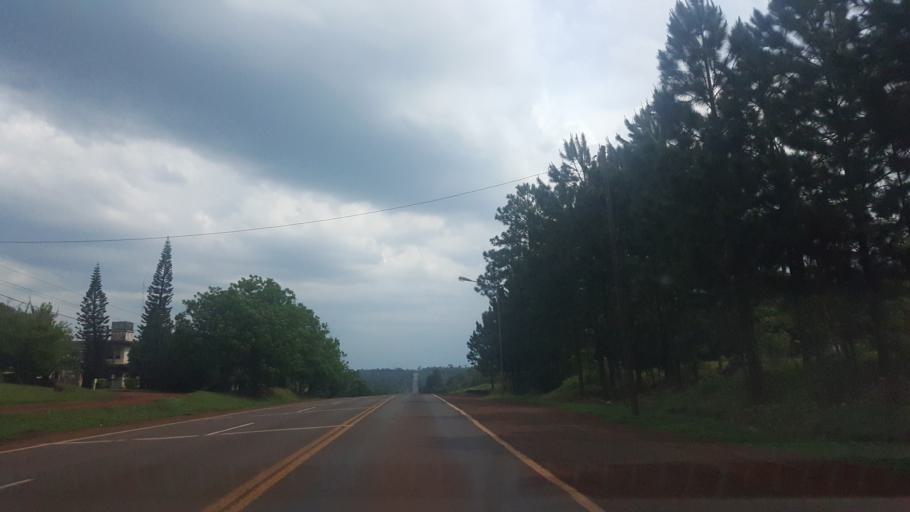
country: AR
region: Misiones
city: Jardin America
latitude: -27.0843
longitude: -55.2876
